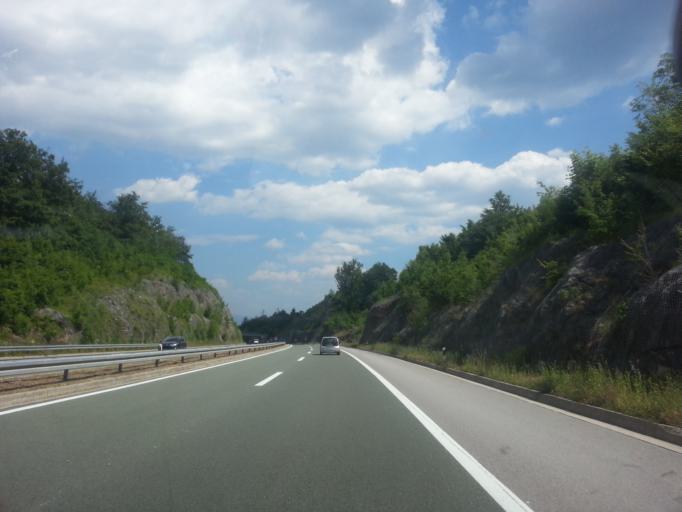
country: HR
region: Primorsko-Goranska
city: Matulji
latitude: 45.3809
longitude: 14.3073
